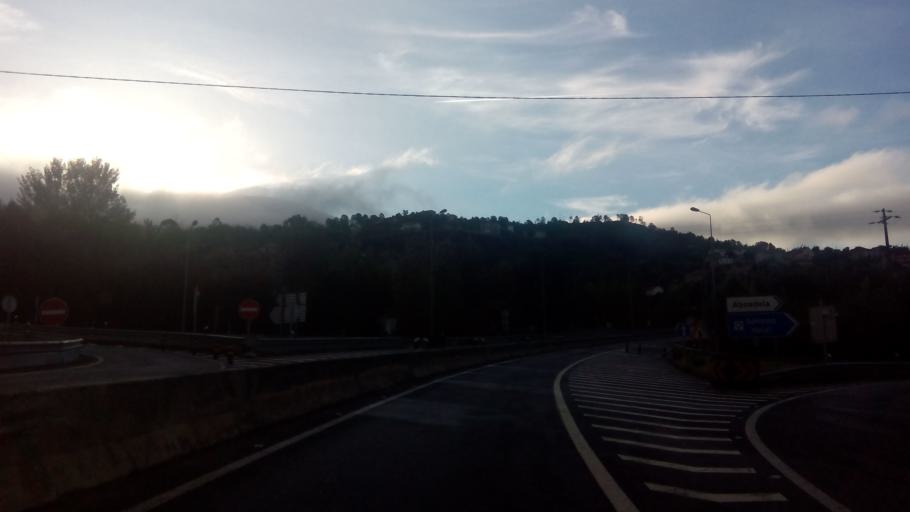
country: PT
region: Porto
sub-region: Amarante
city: Amarante
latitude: 41.2810
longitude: -7.9930
